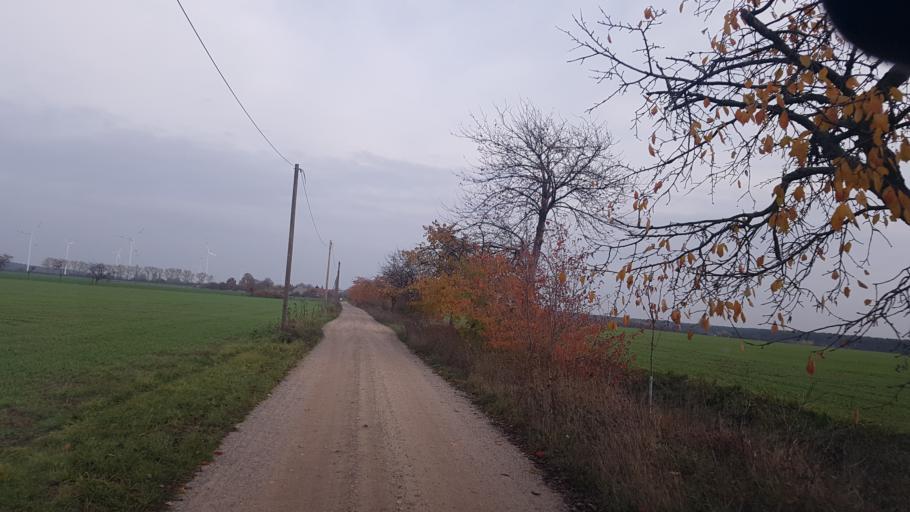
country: DE
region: Brandenburg
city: Trobitz
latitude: 51.6612
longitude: 13.4185
